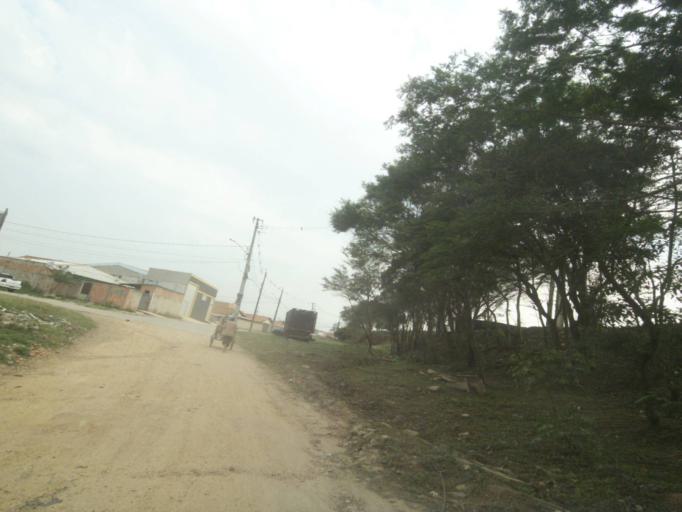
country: BR
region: Parana
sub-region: Sao Jose Dos Pinhais
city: Sao Jose dos Pinhais
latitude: -25.5319
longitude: -49.2303
